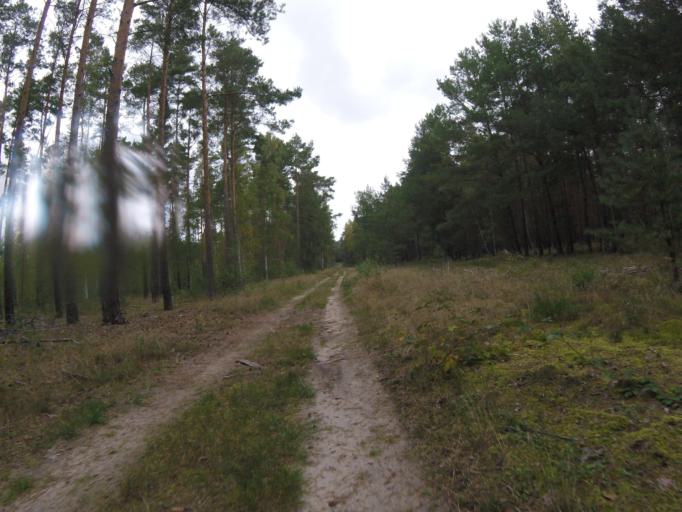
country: DE
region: Brandenburg
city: Gross Koris
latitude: 52.1923
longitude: 13.6745
